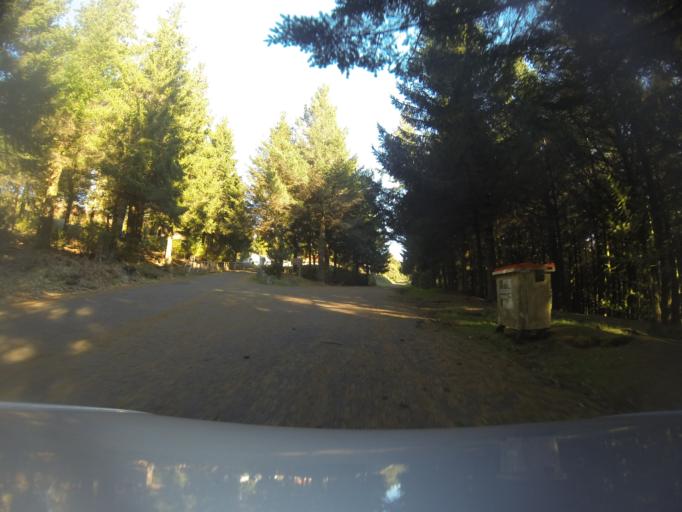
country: PT
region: Madeira
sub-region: Sao Vicente
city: Sao Vicente
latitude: 32.7709
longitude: -17.0767
